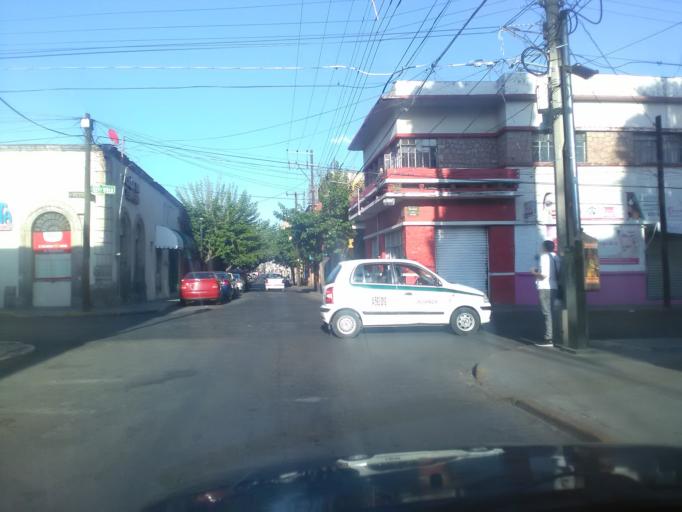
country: MX
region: Durango
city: Victoria de Durango
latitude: 24.0223
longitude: -104.6690
